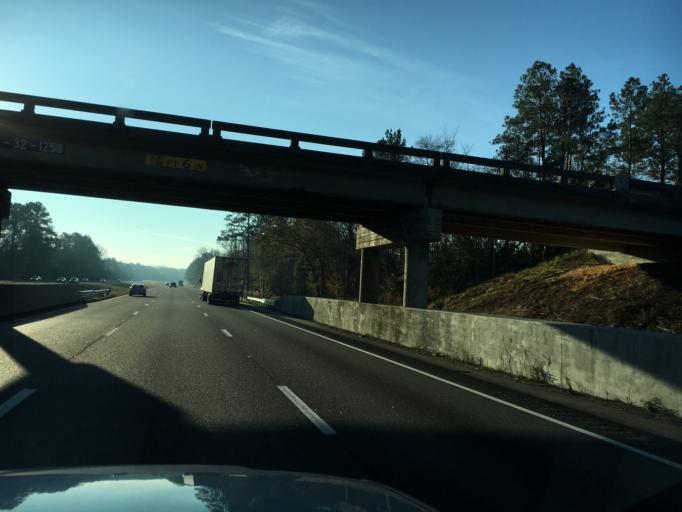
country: US
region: South Carolina
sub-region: Lexington County
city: Pineridge
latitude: 33.8937
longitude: -81.0435
